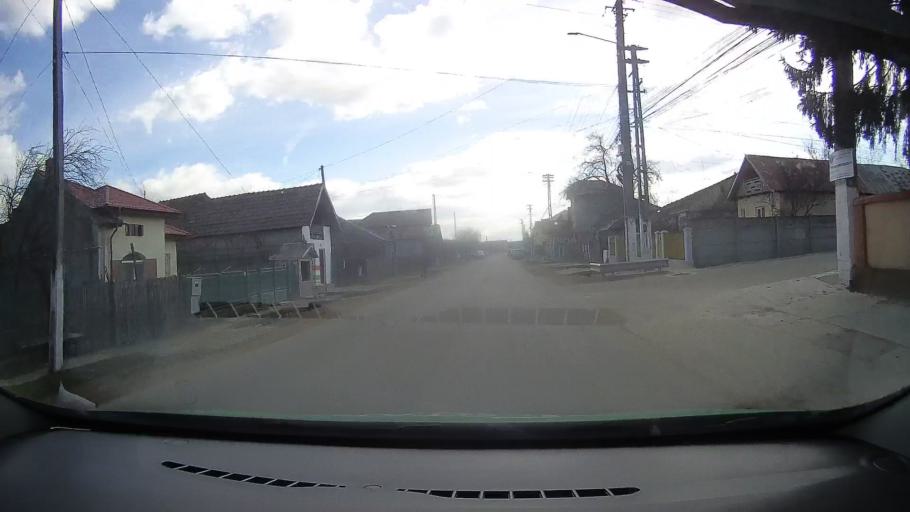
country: RO
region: Dambovita
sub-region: Comuna Doicesti
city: Doicesti
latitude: 44.9813
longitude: 25.3892
